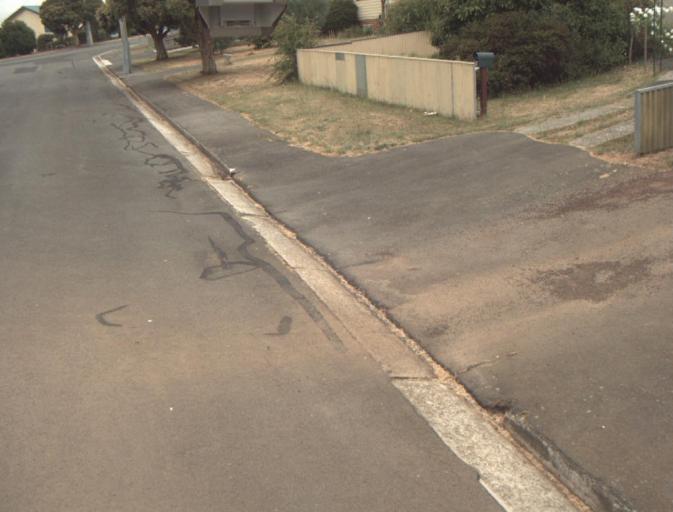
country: AU
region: Tasmania
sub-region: Launceston
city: Newstead
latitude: -41.4327
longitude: 147.1849
